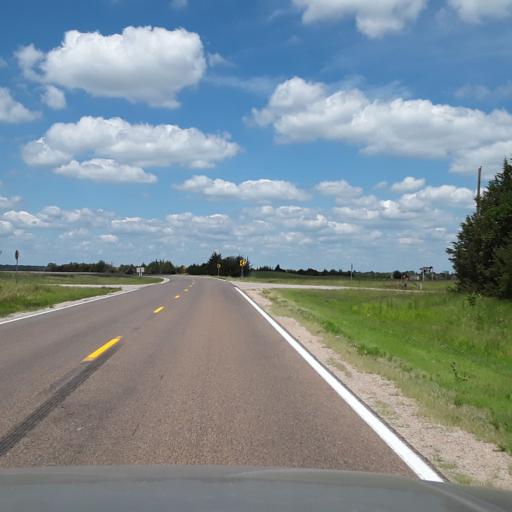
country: US
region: Nebraska
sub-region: Nance County
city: Genoa
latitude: 41.3943
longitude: -97.6942
